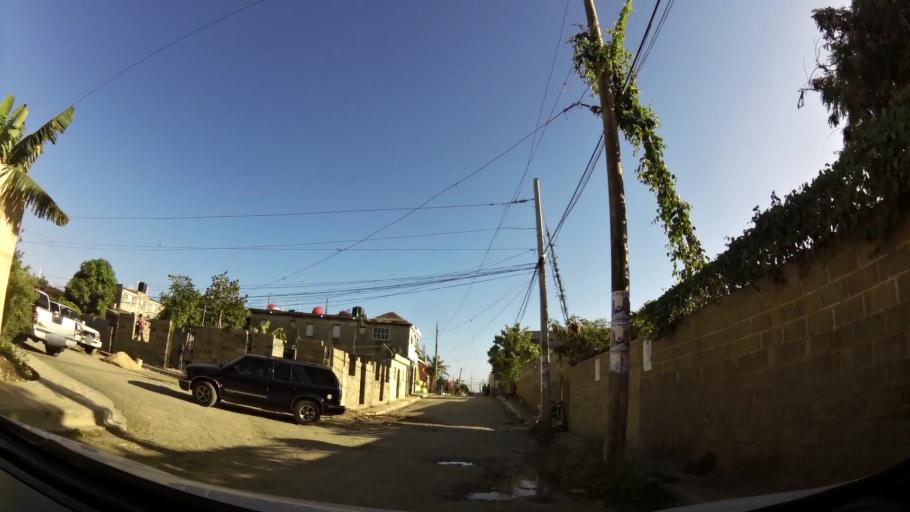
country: DO
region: Santo Domingo
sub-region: Santo Domingo
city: Santo Domingo Este
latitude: 18.4799
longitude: -69.8234
